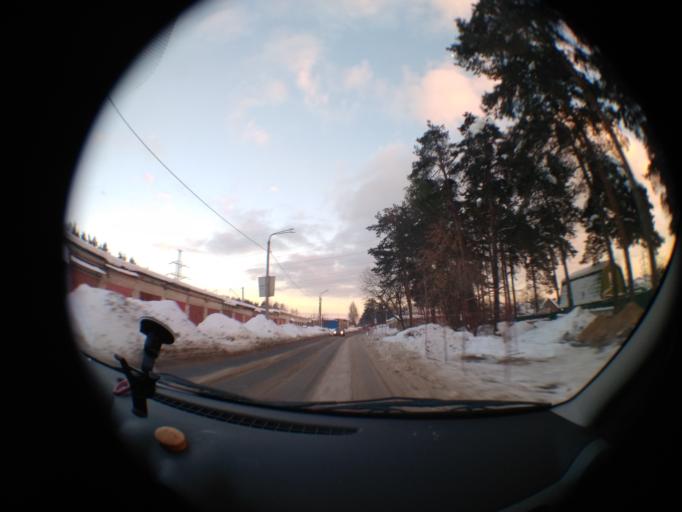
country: RU
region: Moskovskaya
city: Zhukovskiy
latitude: 55.6047
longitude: 38.1281
